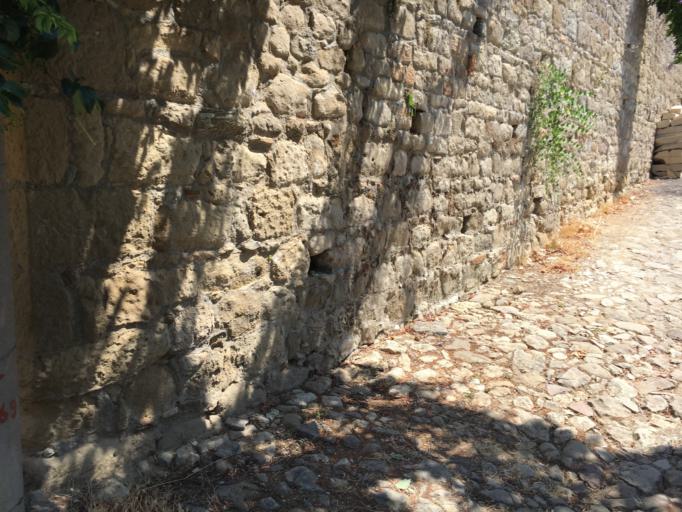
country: TR
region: Canakkale
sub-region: Merkez
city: Kucukkuyu
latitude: 39.5704
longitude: 26.6196
